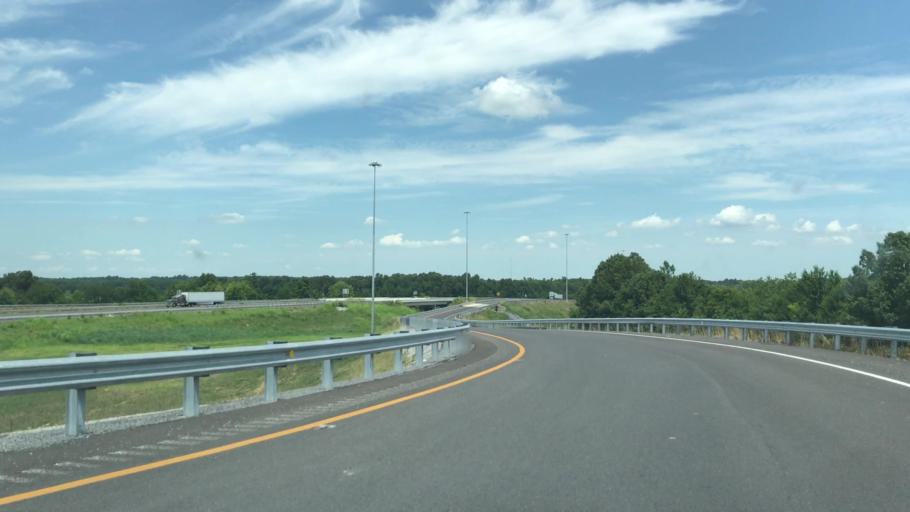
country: US
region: Kentucky
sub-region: Marshall County
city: Benton
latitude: 36.8685
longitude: -88.3635
